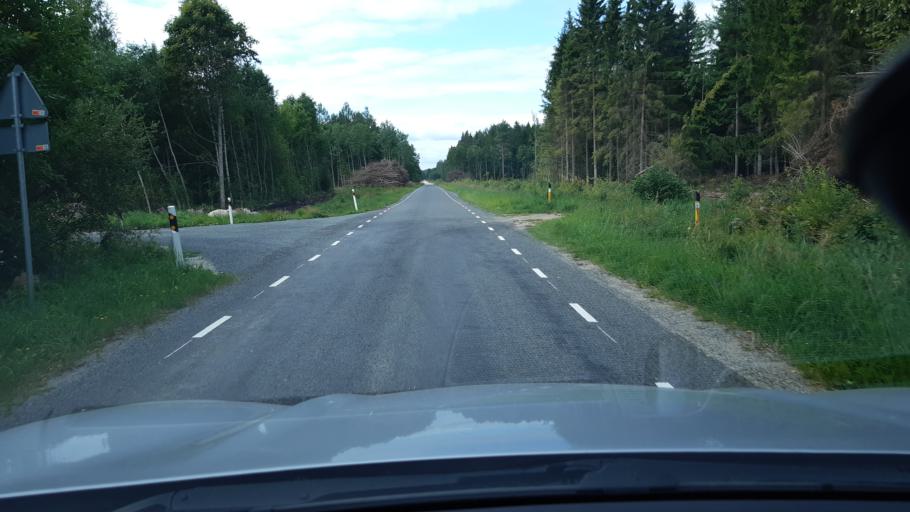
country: EE
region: Raplamaa
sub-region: Jaervakandi vald
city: Jarvakandi
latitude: 58.7511
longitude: 24.9160
